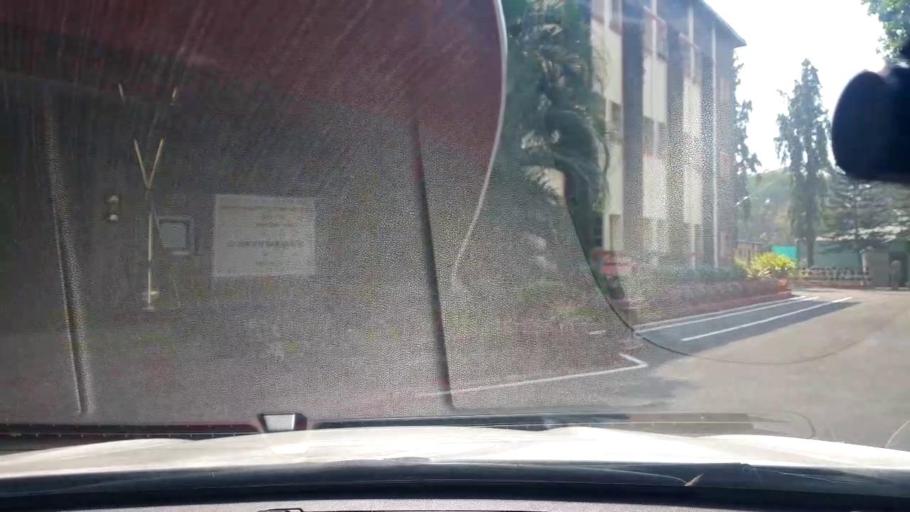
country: IN
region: Maharashtra
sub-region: Pune Division
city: Khadki
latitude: 18.5501
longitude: 73.8637
